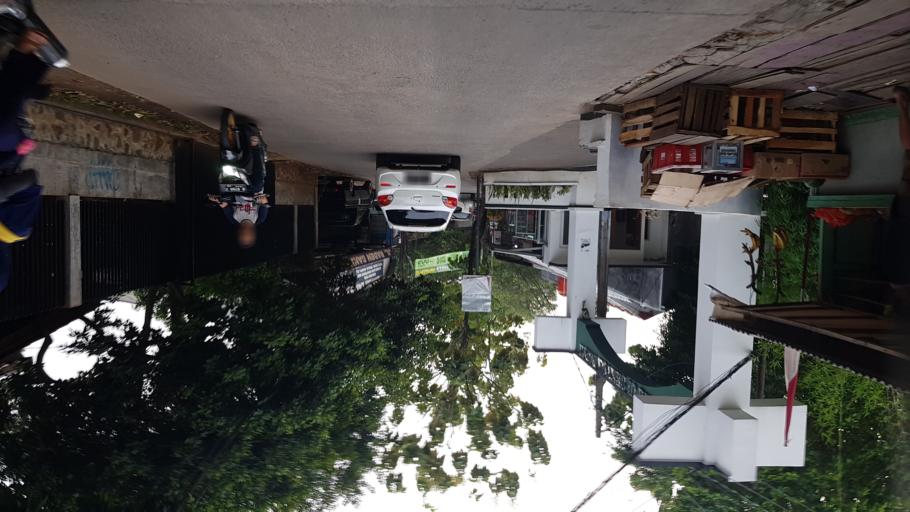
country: ID
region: West Java
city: Depok
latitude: -6.3811
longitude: 106.8023
